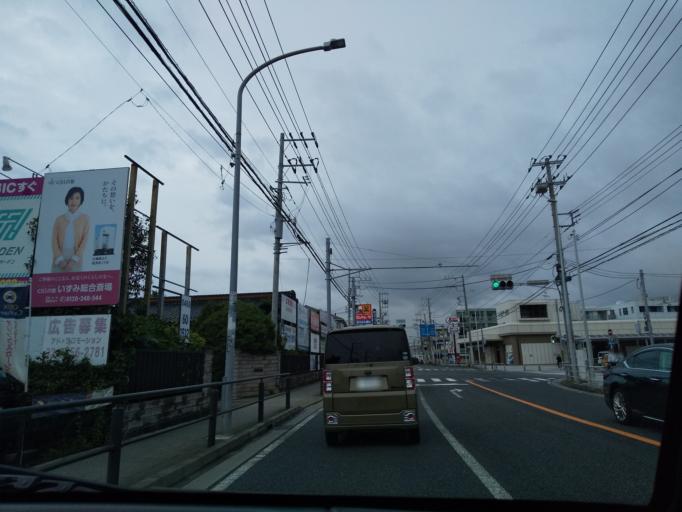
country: JP
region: Kanagawa
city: Fujisawa
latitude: 35.4134
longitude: 139.4996
